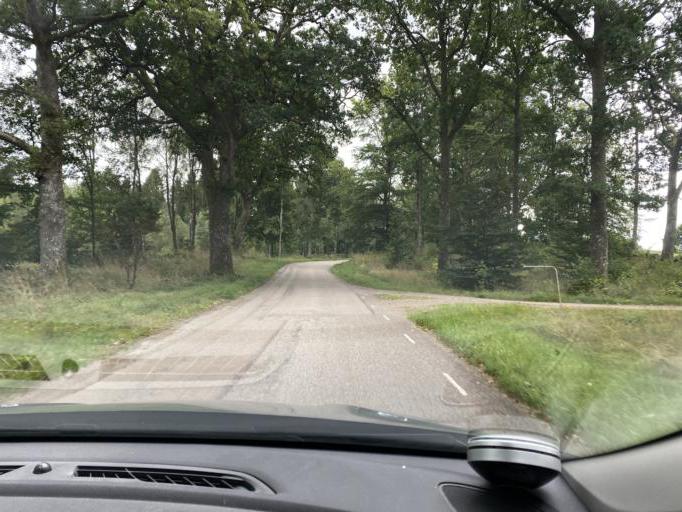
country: SE
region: Kronoberg
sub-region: Markaryds Kommun
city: Markaryd
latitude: 56.4815
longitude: 13.5645
